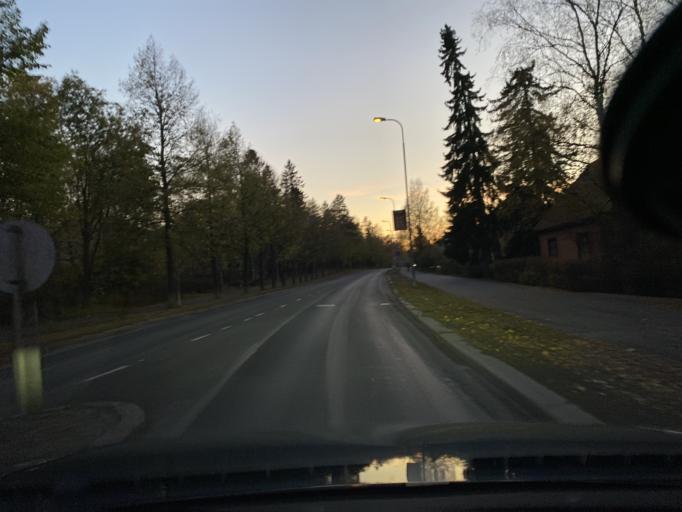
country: FI
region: Pirkanmaa
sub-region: Tampere
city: Tampere
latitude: 61.4711
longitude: 23.7544
